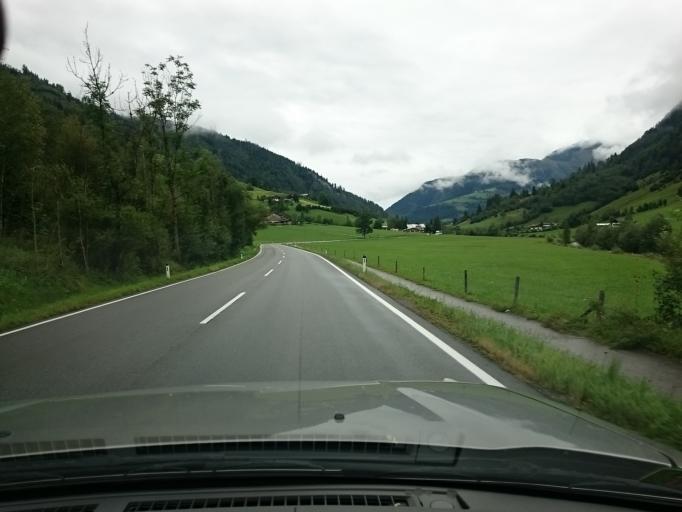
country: AT
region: Salzburg
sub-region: Politischer Bezirk Zell am See
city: Bruck an der Grossglocknerstrasse
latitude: 47.2524
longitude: 12.8245
